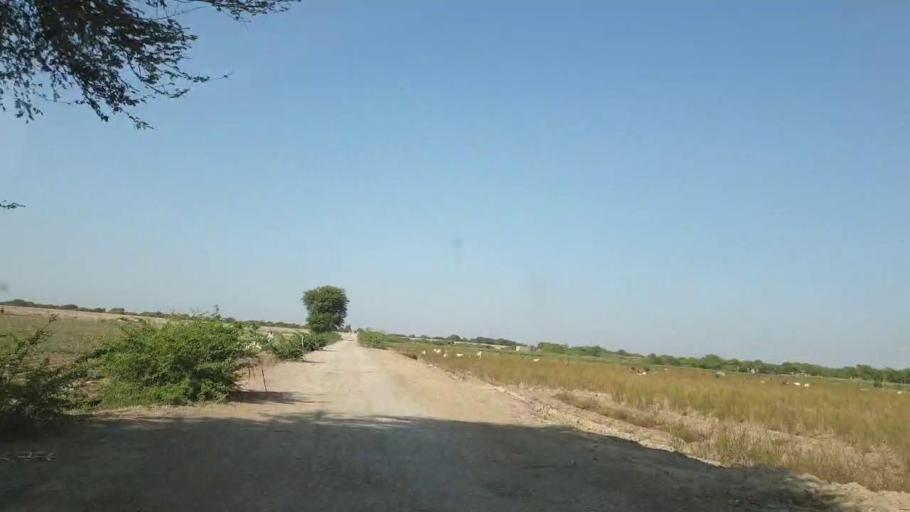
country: PK
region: Sindh
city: Nabisar
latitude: 25.0297
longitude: 69.4864
